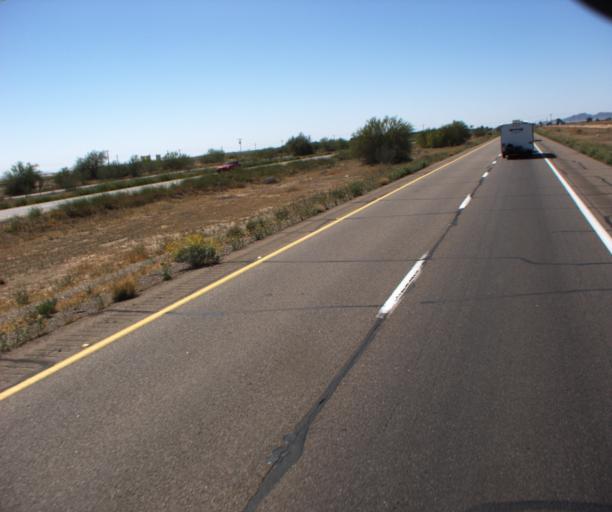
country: US
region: Arizona
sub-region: Maricopa County
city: Gila Bend
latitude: 32.9248
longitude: -112.8665
